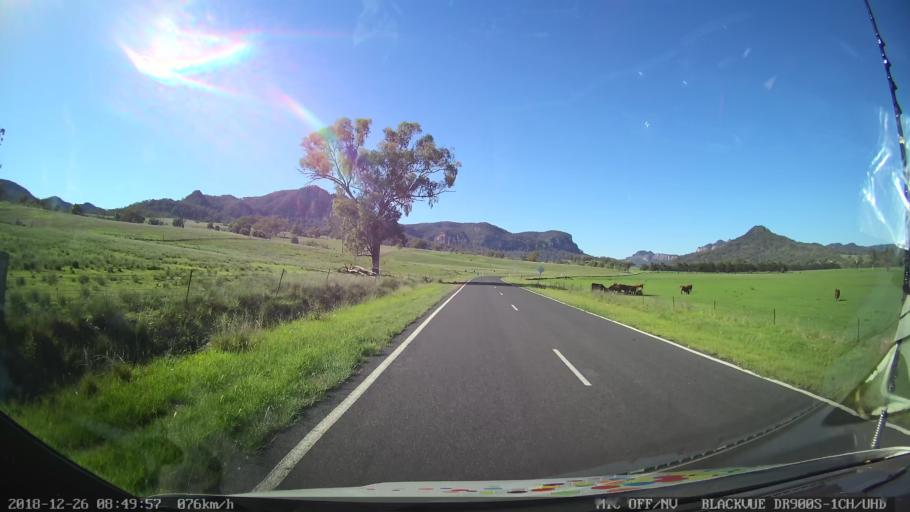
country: AU
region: New South Wales
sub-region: Mid-Western Regional
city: Kandos
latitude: -32.5703
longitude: 150.0972
